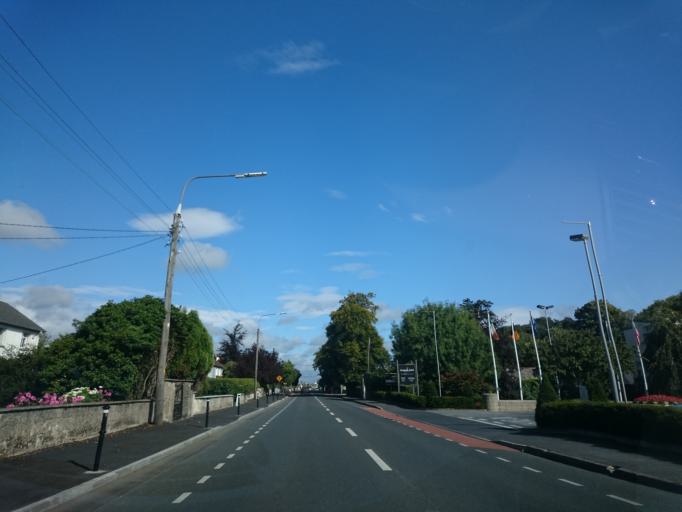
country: IE
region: Leinster
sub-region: Kilkenny
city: Kilkenny
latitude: 52.6643
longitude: -7.2514
